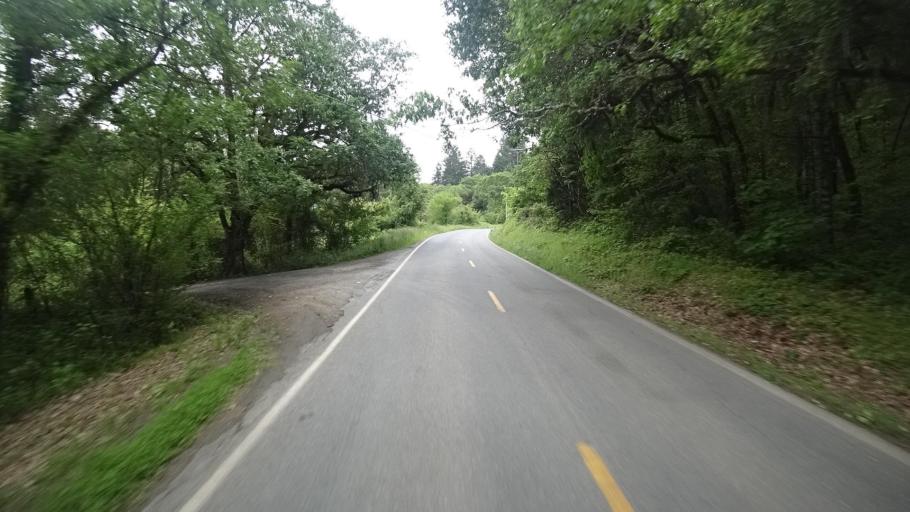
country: US
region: California
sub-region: Humboldt County
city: Willow Creek
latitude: 41.0707
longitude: -123.6946
